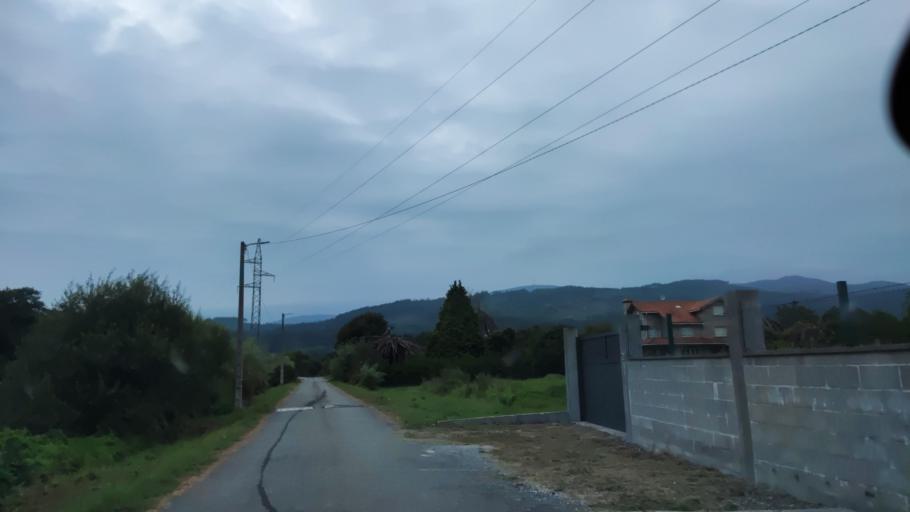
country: ES
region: Galicia
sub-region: Provincia da Coruna
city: Rois
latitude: 42.7146
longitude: -8.7056
